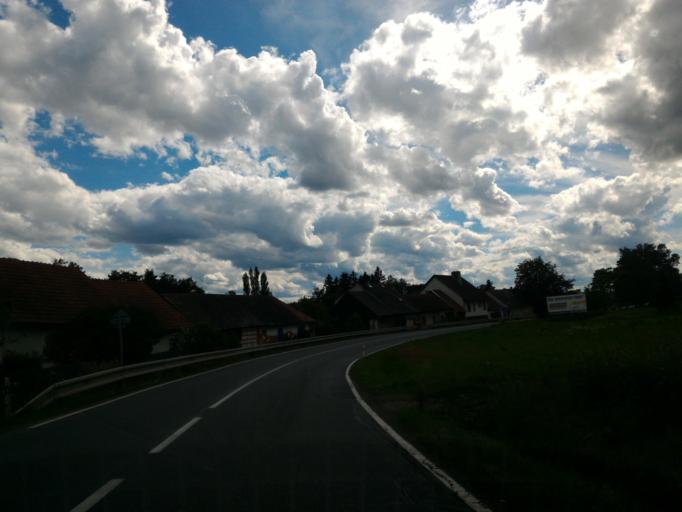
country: CZ
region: Vysocina
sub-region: Okres Jihlava
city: Polna
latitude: 49.4463
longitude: 15.7753
